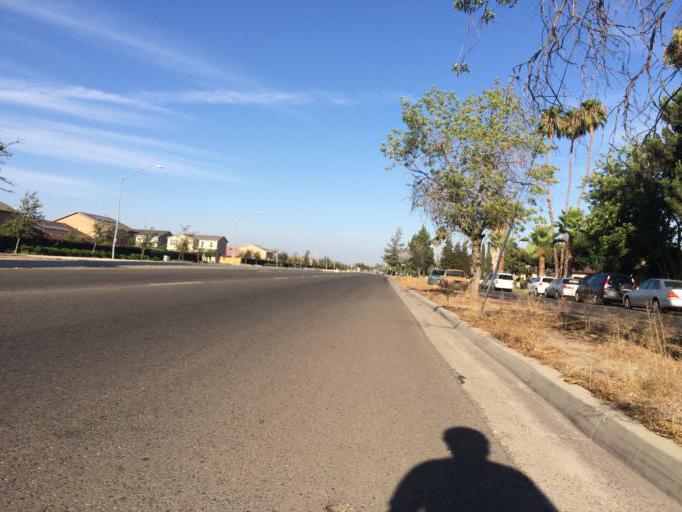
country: US
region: California
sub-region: Fresno County
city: Sunnyside
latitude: 36.7362
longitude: -119.6911
